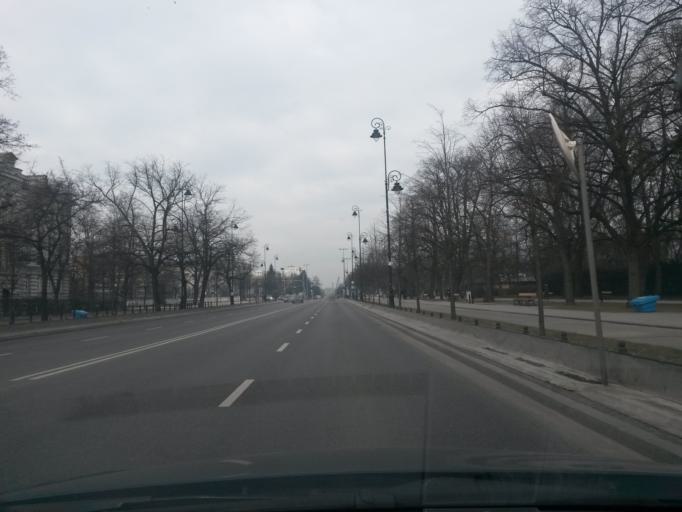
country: PL
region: Masovian Voivodeship
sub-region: Warszawa
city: Srodmiescie
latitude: 52.2177
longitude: 21.0258
